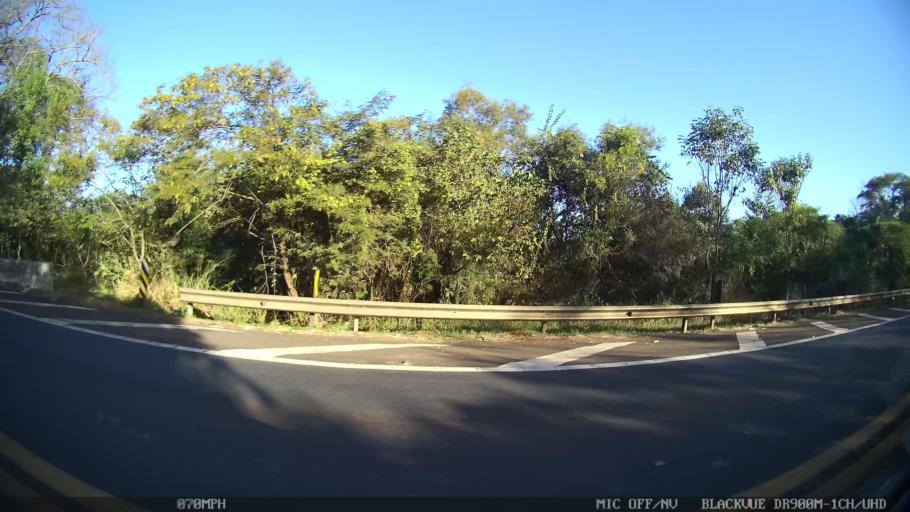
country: BR
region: Sao Paulo
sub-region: Guapiacu
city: Guapiacu
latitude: -20.7432
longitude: -49.1058
